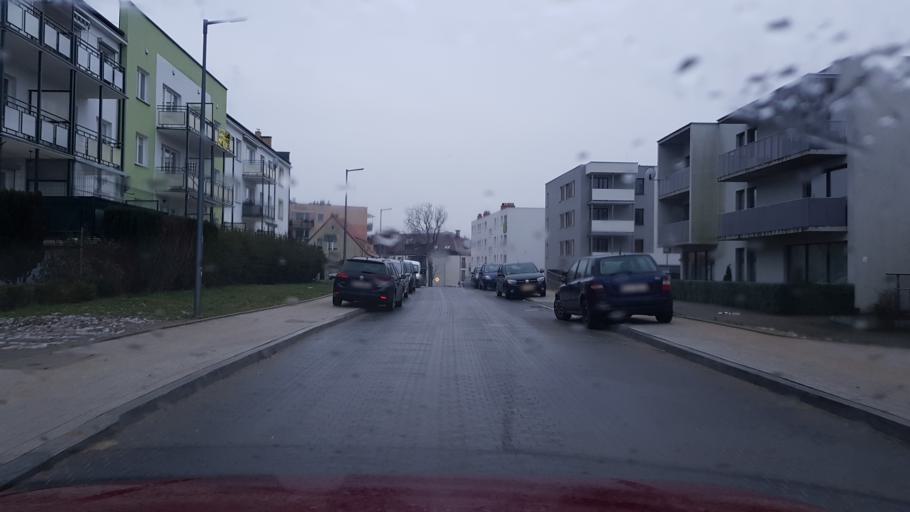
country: PL
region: West Pomeranian Voivodeship
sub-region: Koszalin
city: Koszalin
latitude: 54.1963
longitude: 16.1815
